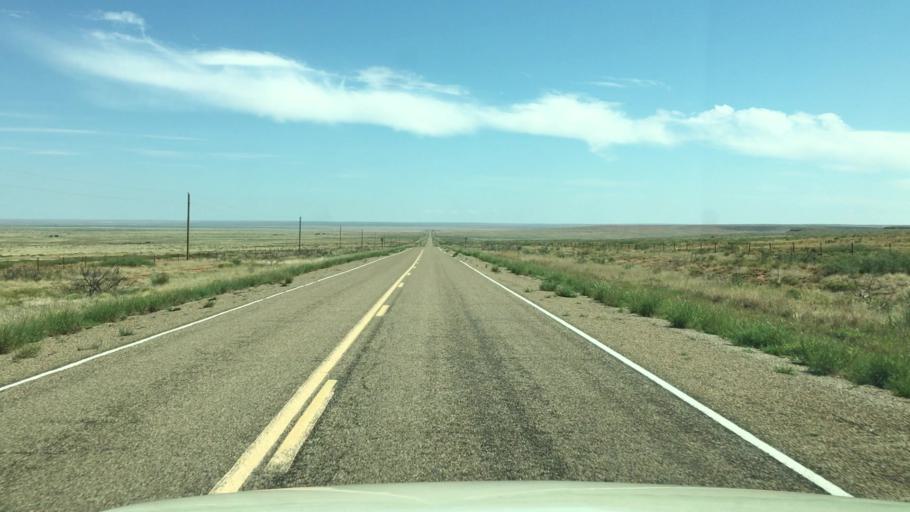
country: US
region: New Mexico
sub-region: Chaves County
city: Roswell
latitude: 33.9779
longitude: -104.5761
